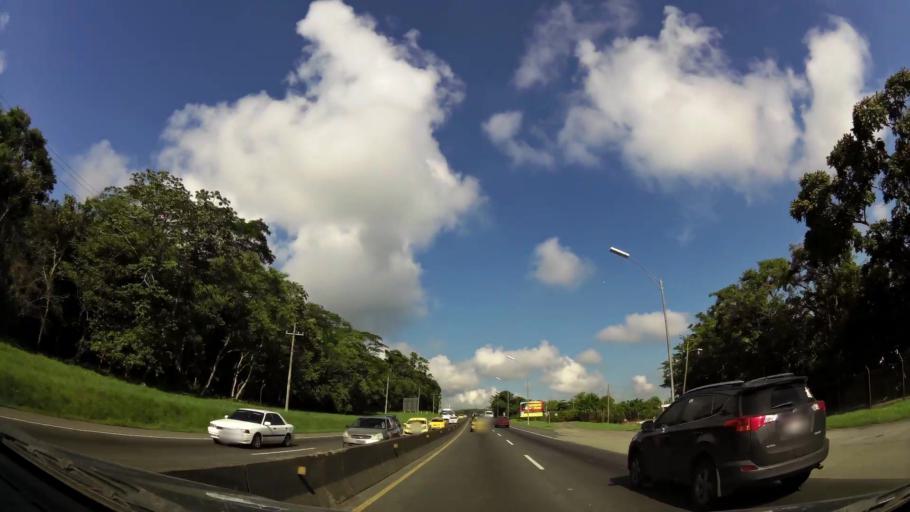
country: PA
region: Panama
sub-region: Distrito de Panama
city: Ancon
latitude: 8.9499
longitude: -79.5855
